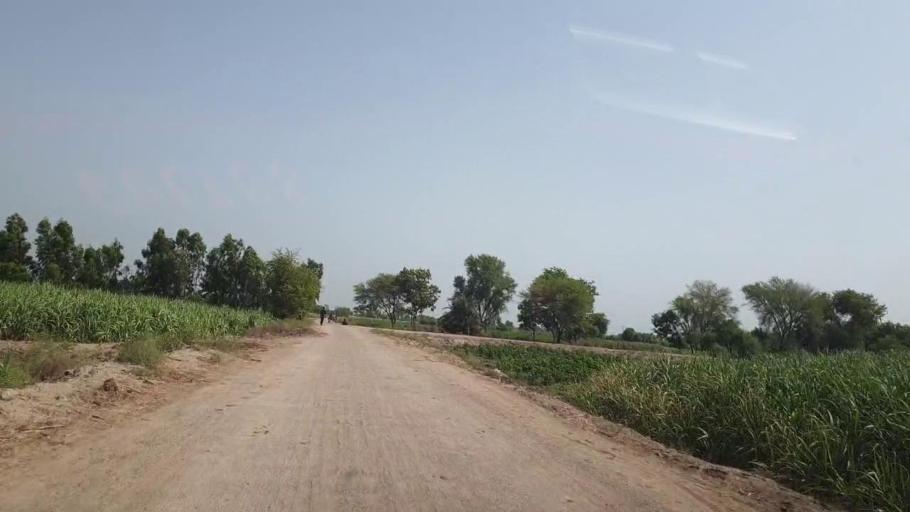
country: PK
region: Sindh
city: Daur
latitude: 26.3164
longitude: 68.2155
